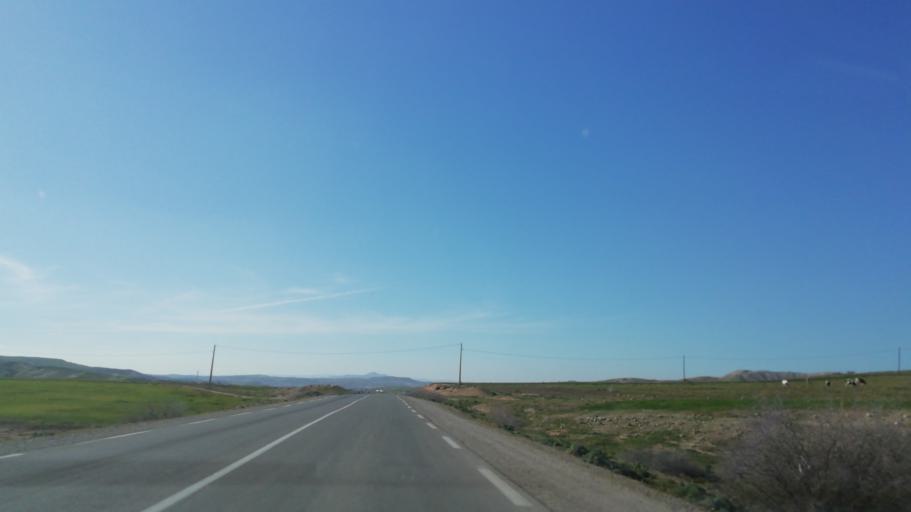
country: DZ
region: Mascara
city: Oued el Abtal
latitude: 35.4545
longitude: 0.7686
